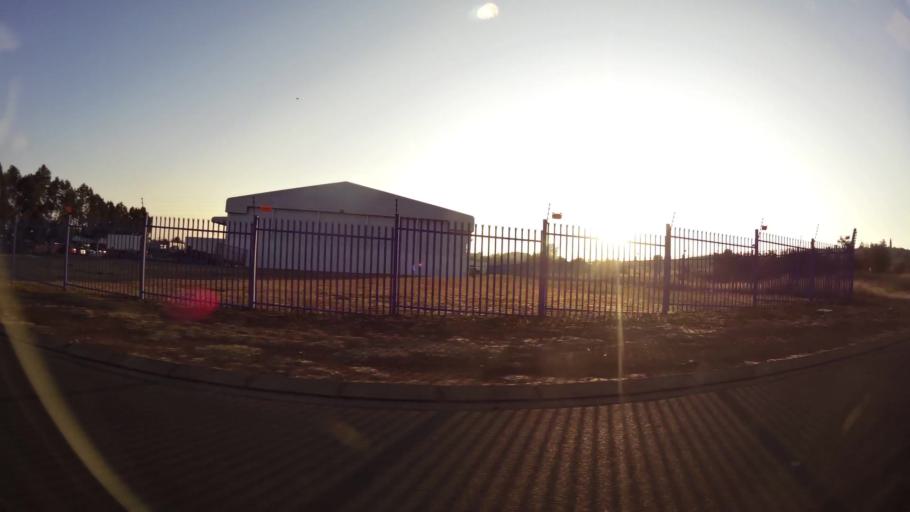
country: ZA
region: Orange Free State
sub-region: Mangaung Metropolitan Municipality
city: Bloemfontein
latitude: -29.0867
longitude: 26.1619
